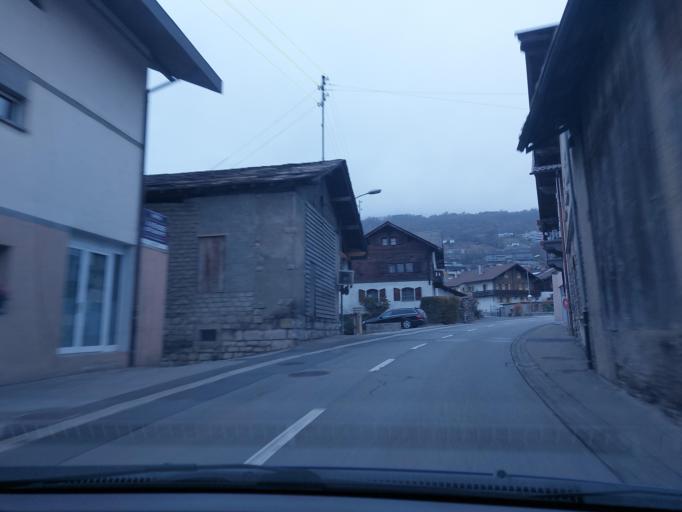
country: CH
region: Valais
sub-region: Sion District
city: Saviese
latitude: 46.2473
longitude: 7.3479
